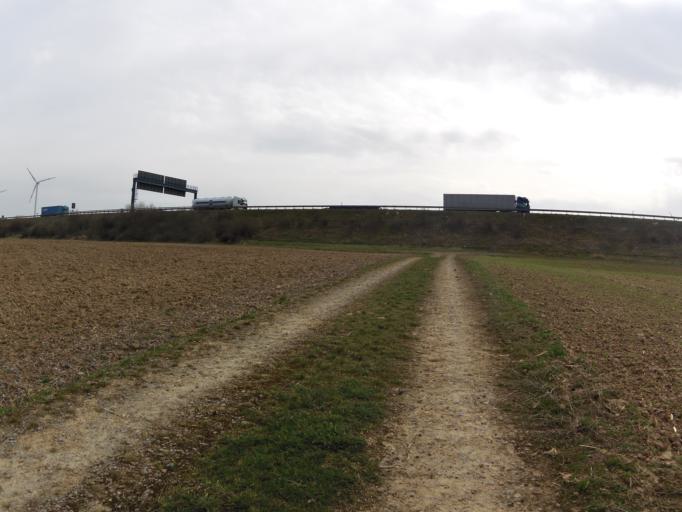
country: DE
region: Bavaria
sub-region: Regierungsbezirk Unterfranken
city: Biebelried
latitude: 49.7832
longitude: 10.1033
